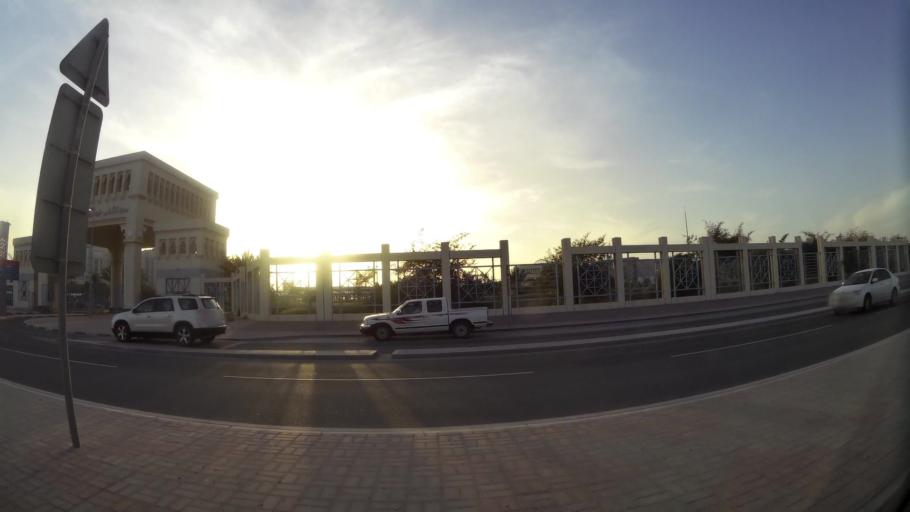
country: QA
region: Al Wakrah
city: Al Wakrah
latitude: 25.1686
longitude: 51.5910
